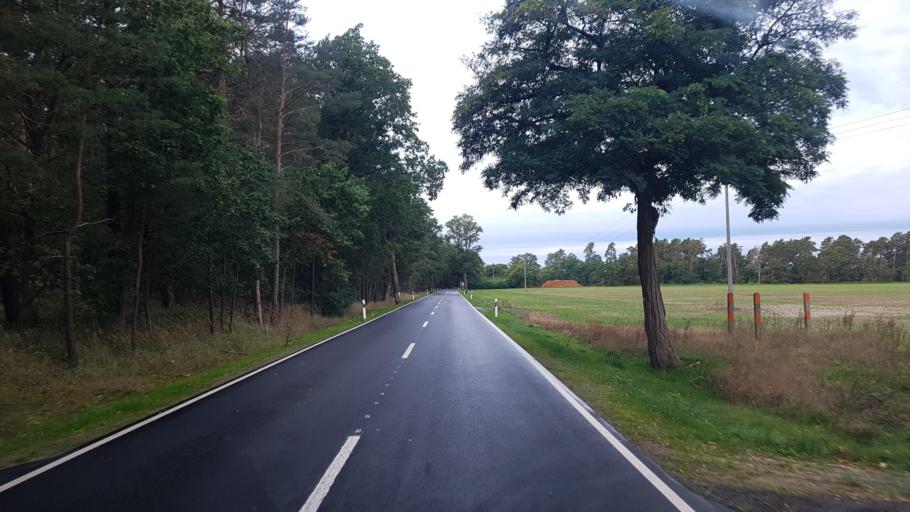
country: DE
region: Brandenburg
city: Kasel-Golzig
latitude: 51.9353
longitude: 13.7258
